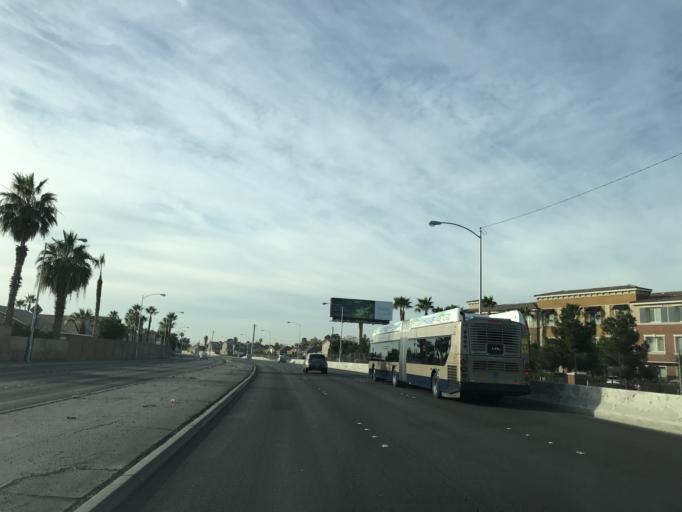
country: US
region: Nevada
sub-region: Clark County
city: Sunrise Manor
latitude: 36.1533
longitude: -115.0644
